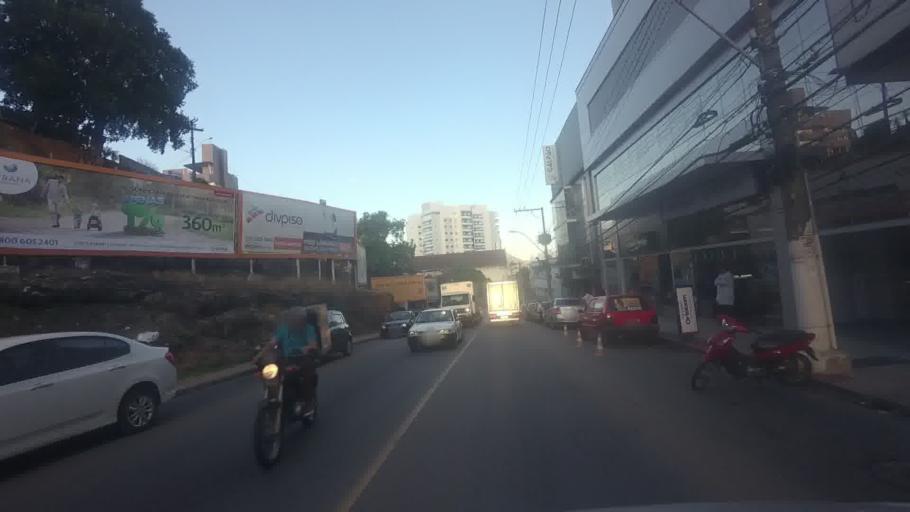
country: BR
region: Espirito Santo
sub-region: Cachoeiro De Itapemirim
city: Cachoeiro de Itapemirim
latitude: -20.8450
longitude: -41.1239
